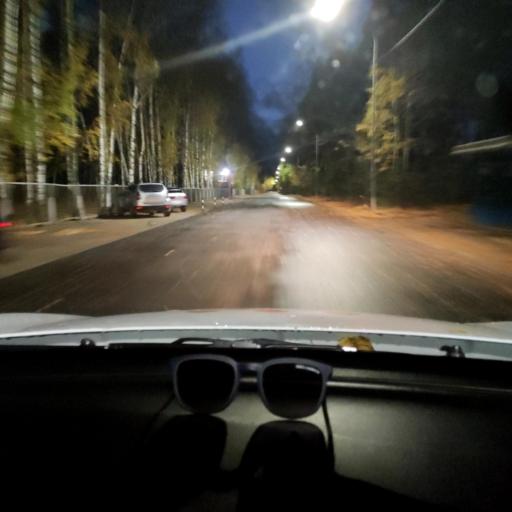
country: RU
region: Tatarstan
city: Verkhniy Uslon
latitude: 55.6034
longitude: 49.0207
